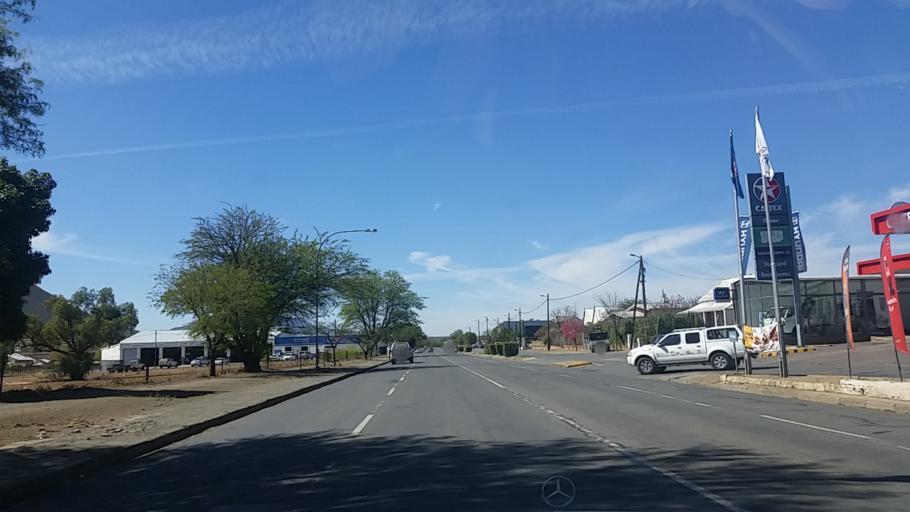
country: ZA
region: Eastern Cape
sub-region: Cacadu District Municipality
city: Graaff-Reinet
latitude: -32.2645
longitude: 24.5415
